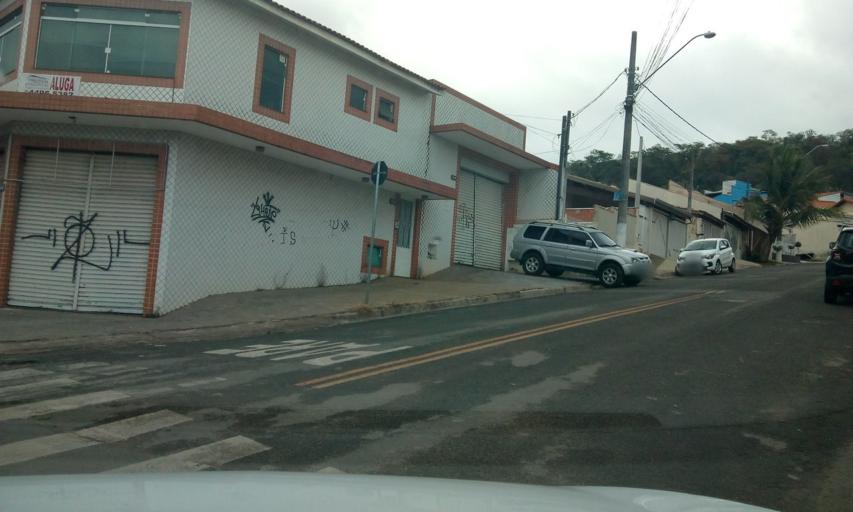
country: BR
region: Sao Paulo
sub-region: Itupeva
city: Itupeva
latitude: -23.1555
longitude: -47.0627
